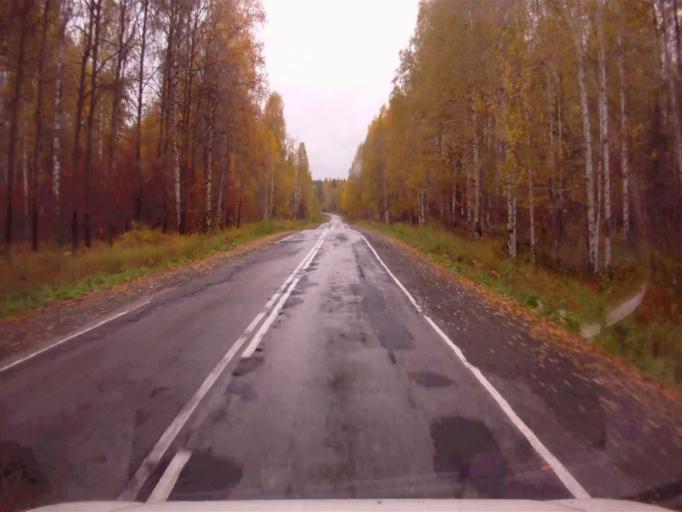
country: RU
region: Chelyabinsk
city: Nizhniy Ufaley
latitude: 56.0546
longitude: 59.9567
